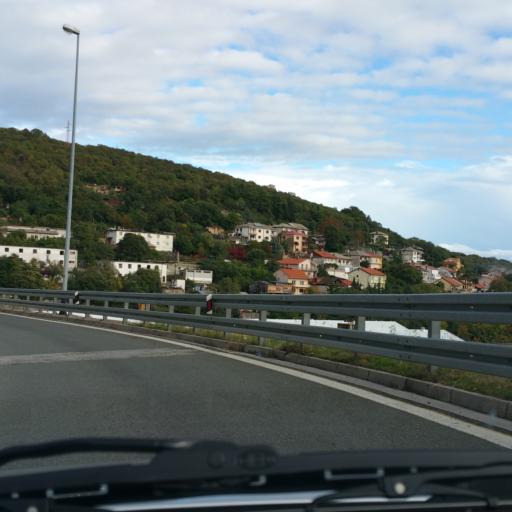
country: HR
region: Primorsko-Goranska
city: Drenova
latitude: 45.3435
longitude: 14.4211
